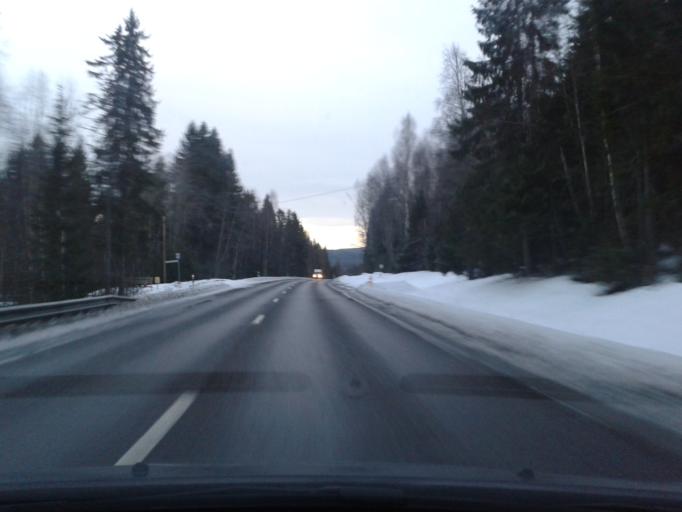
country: SE
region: Vaesternorrland
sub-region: Kramfors Kommun
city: Bollstabruk
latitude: 63.0938
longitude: 17.5266
